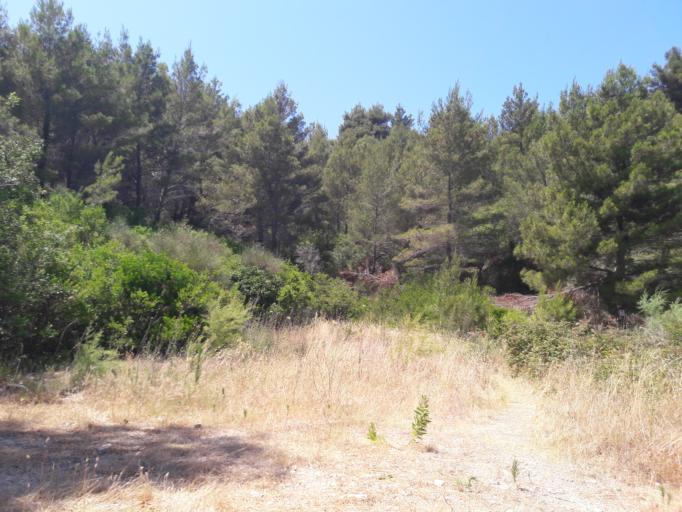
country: HR
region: Sibensko-Kniniska
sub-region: Grad Sibenik
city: Sibenik
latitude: 43.7032
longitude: 15.8457
